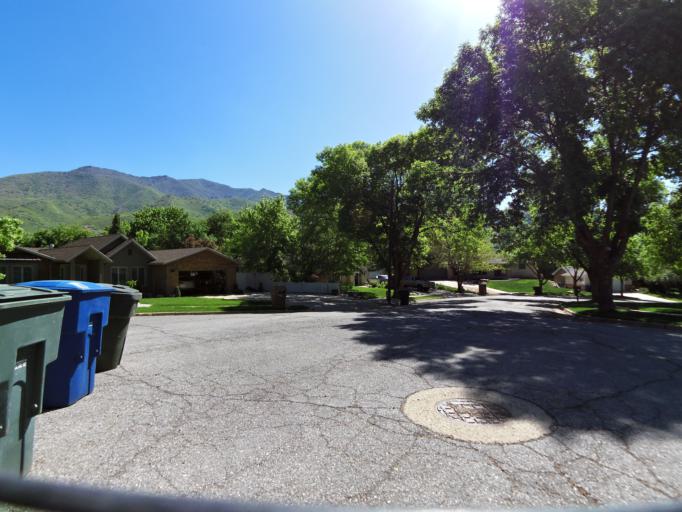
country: US
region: Utah
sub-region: Weber County
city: Uintah
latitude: 41.1669
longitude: -111.9354
